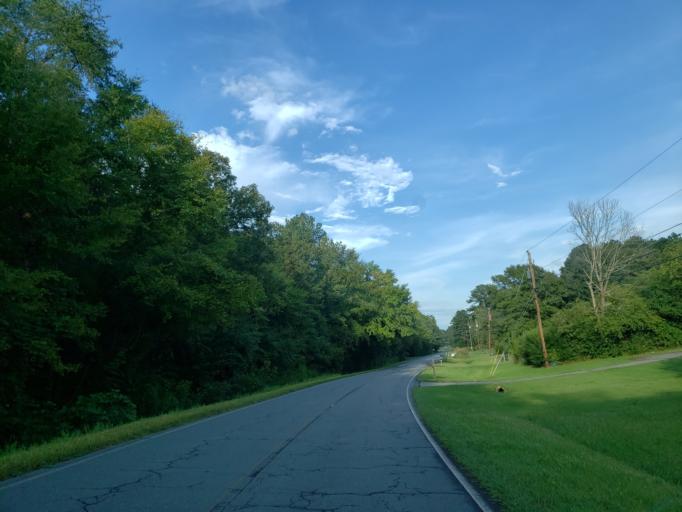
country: US
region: Georgia
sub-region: Bartow County
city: Euharlee
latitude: 34.2278
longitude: -84.9667
